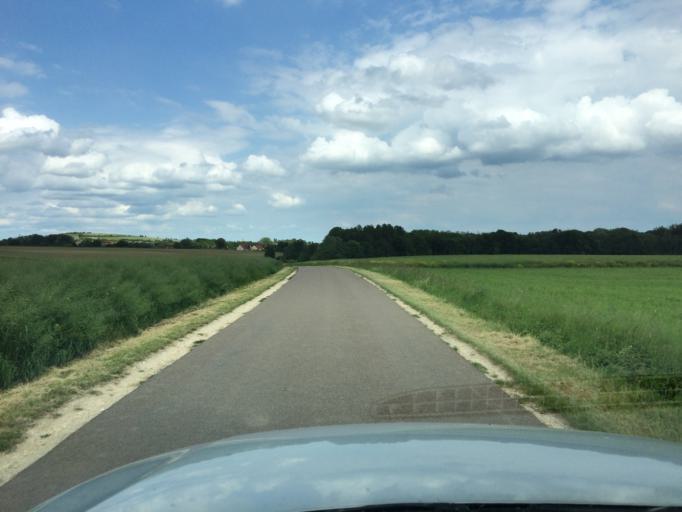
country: FR
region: Bourgogne
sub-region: Departement de l'Yonne
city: Fleury-la-Vallee
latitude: 47.8754
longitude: 3.4020
